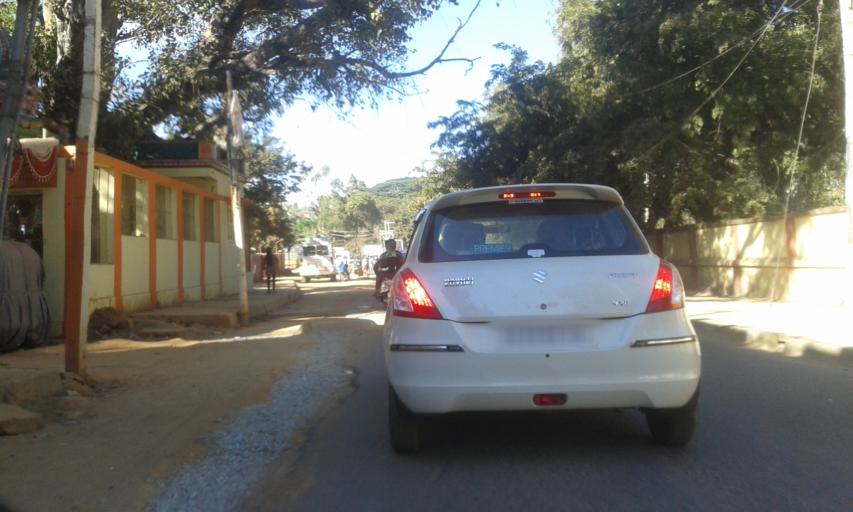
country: IN
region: Karnataka
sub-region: Bangalore Urban
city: Bangalore
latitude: 12.9619
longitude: 77.6170
